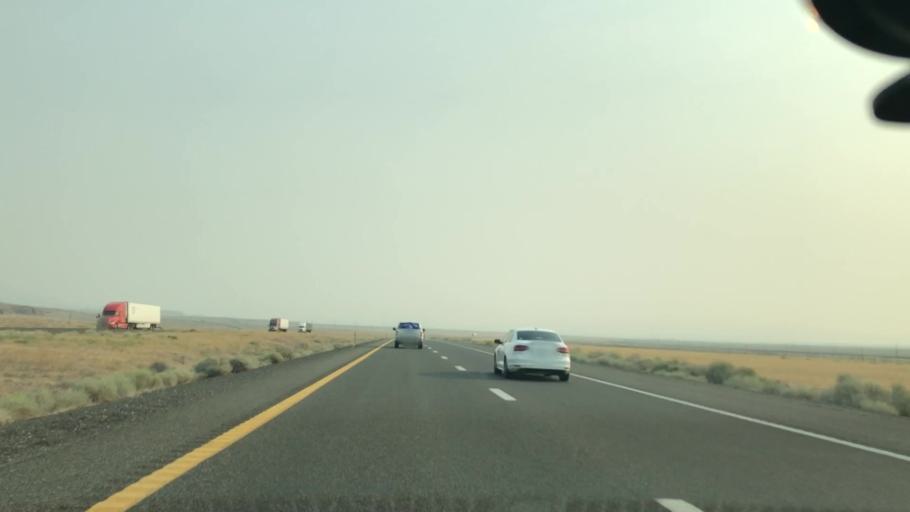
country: US
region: Nevada
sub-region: Pershing County
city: Lovelock
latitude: 40.0185
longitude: -118.6754
